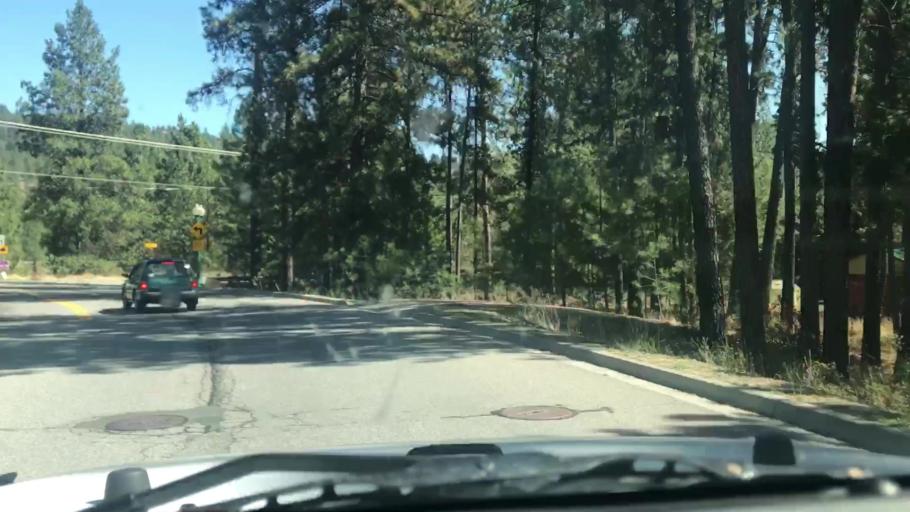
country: US
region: Washington
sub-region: Spokane County
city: Spokane
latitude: 47.5986
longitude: -117.4117
